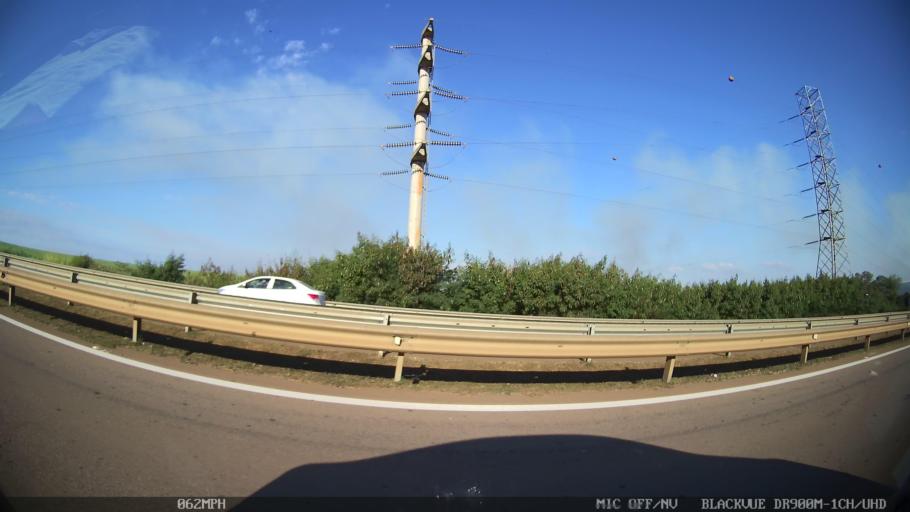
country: BR
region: Sao Paulo
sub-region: Piracicaba
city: Piracicaba
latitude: -22.6856
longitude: -47.5972
